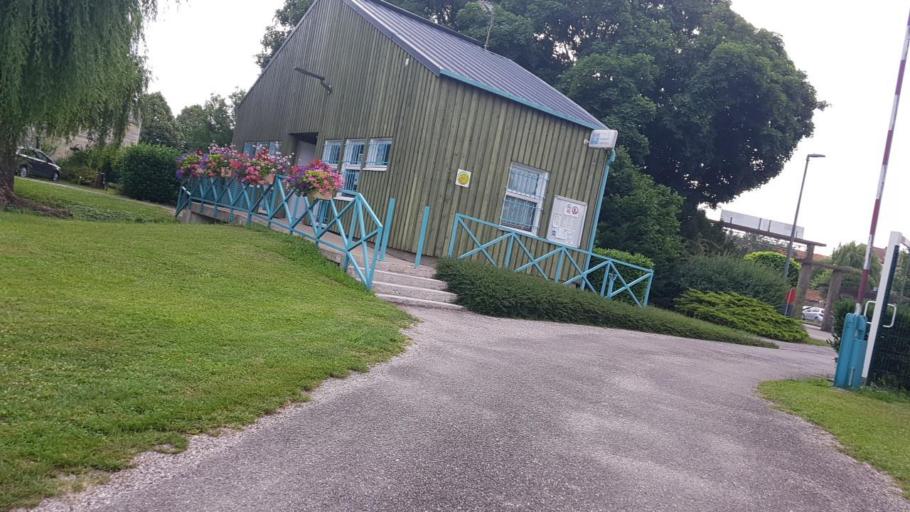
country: FR
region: Lorraine
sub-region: Departement de la Meuse
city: Revigny-sur-Ornain
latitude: 48.8265
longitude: 4.9827
